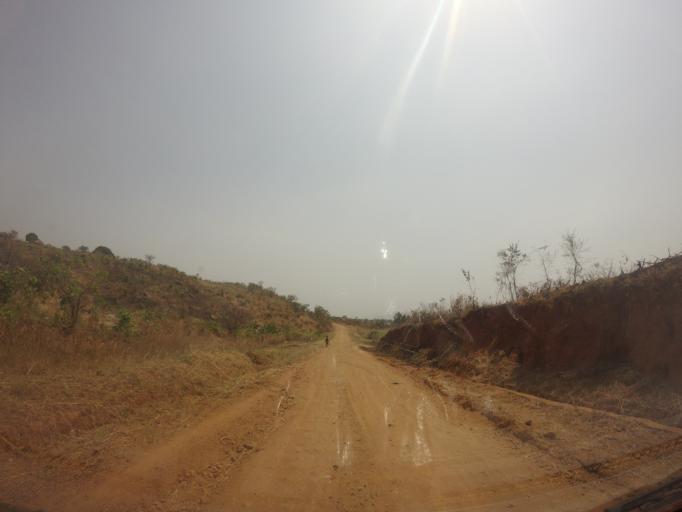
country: UG
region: Northern Region
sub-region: Arua District
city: Arua
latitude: 2.9241
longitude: 30.9910
